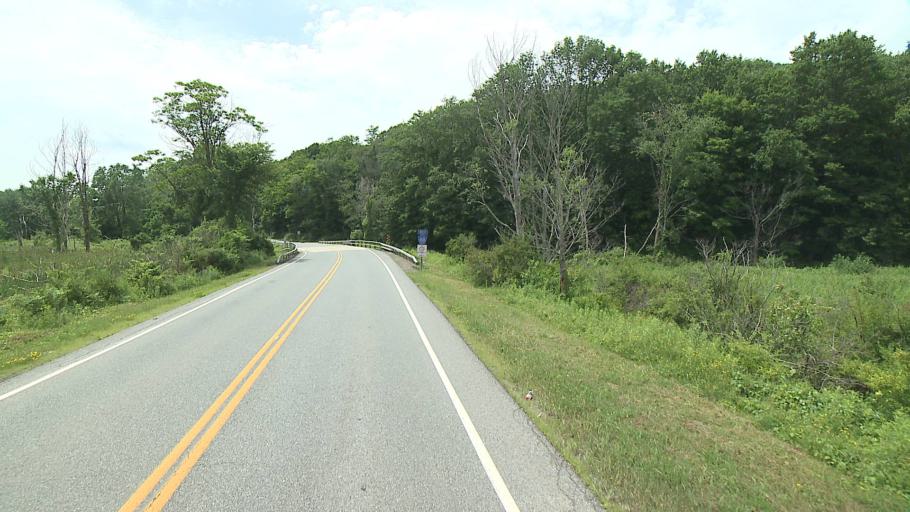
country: US
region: New York
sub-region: Putnam County
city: Putnam Lake
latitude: 41.4987
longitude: -73.5331
